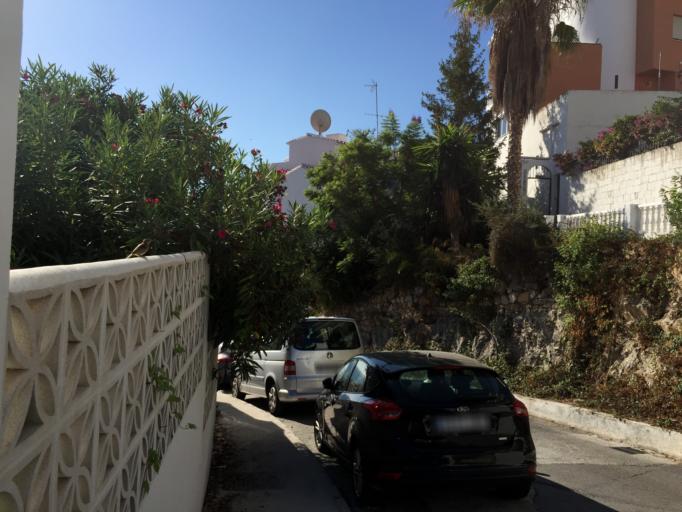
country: ES
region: Andalusia
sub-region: Provincia de Malaga
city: Nerja
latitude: 36.7514
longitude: -3.8709
